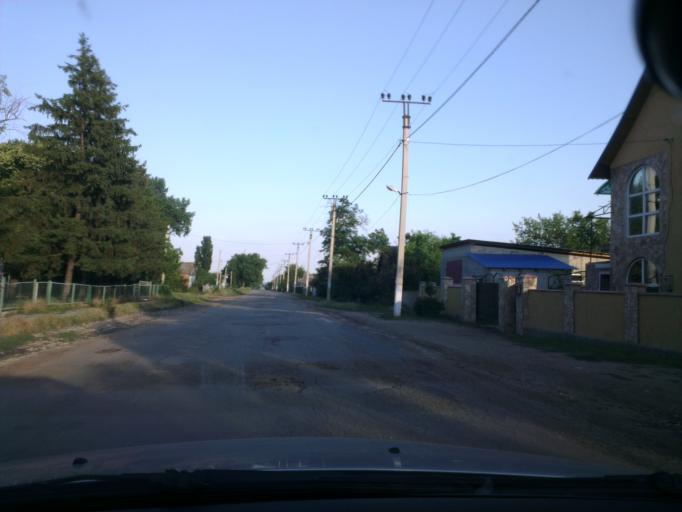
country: MD
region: Cantemir
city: Visniovca
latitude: 46.3534
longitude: 28.4092
